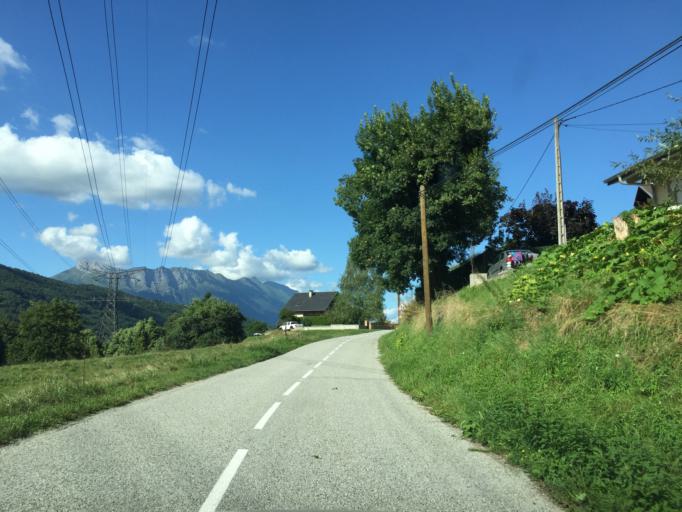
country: FR
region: Rhone-Alpes
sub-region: Departement de la Savoie
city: Coise-Saint-Jean-Pied-Gauthier
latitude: 45.4922
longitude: 6.1585
